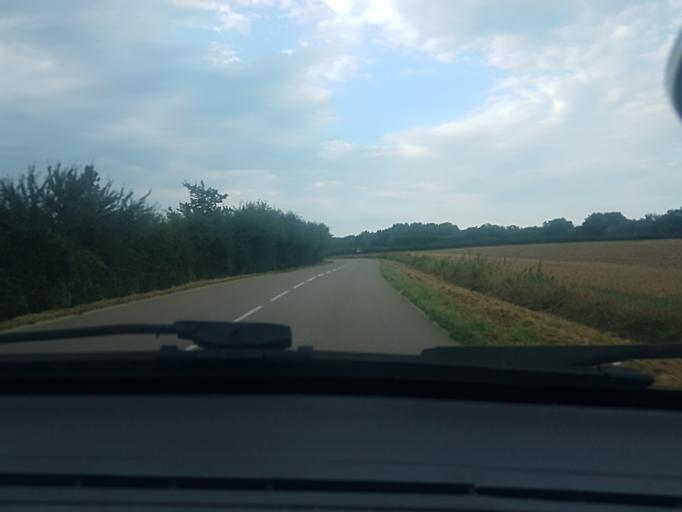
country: FR
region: Bourgogne
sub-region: Departement de Saone-et-Loire
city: Givry
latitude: 46.7373
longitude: 4.7505
